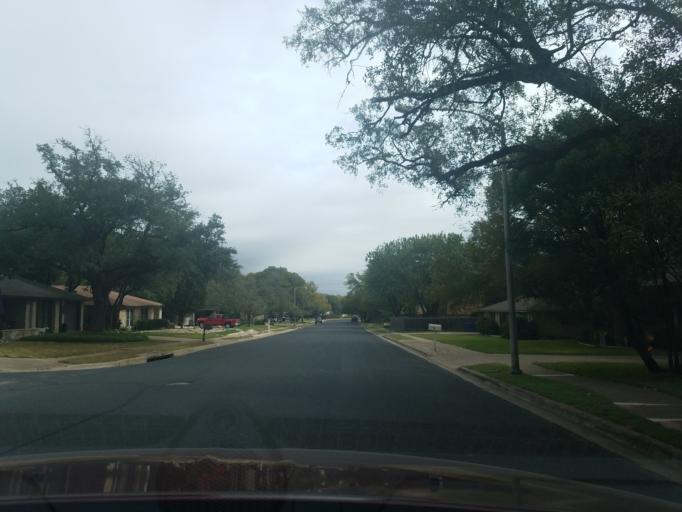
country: US
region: Texas
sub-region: Williamson County
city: Anderson Mill
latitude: 30.4629
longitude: -97.8081
